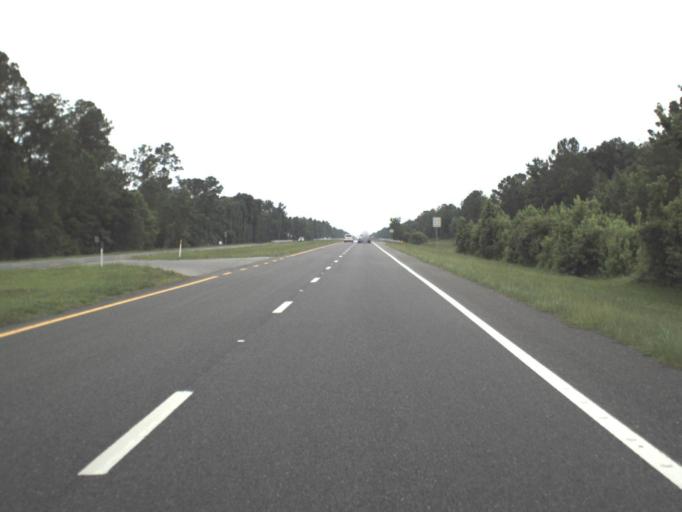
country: US
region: Florida
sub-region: Levy County
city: Chiefland
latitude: 29.3291
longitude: -82.7695
